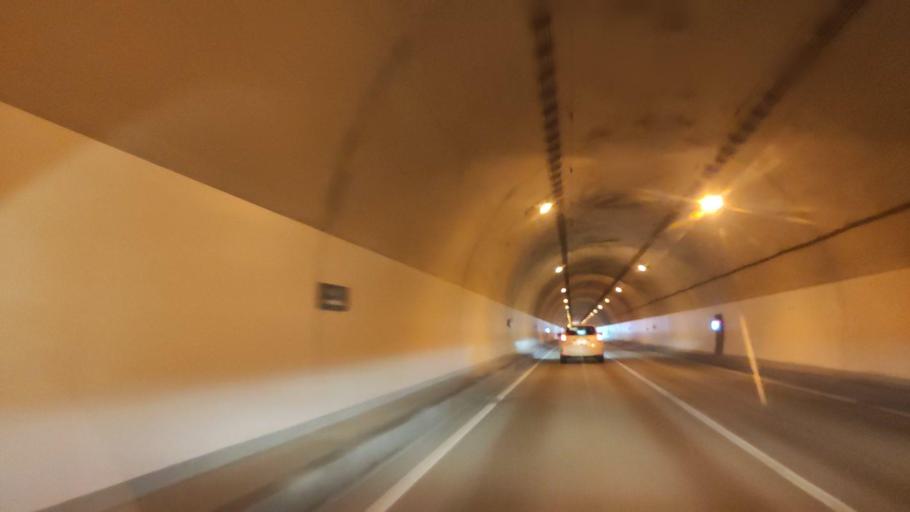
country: JP
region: Hokkaido
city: Ishikari
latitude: 43.4751
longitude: 141.3953
